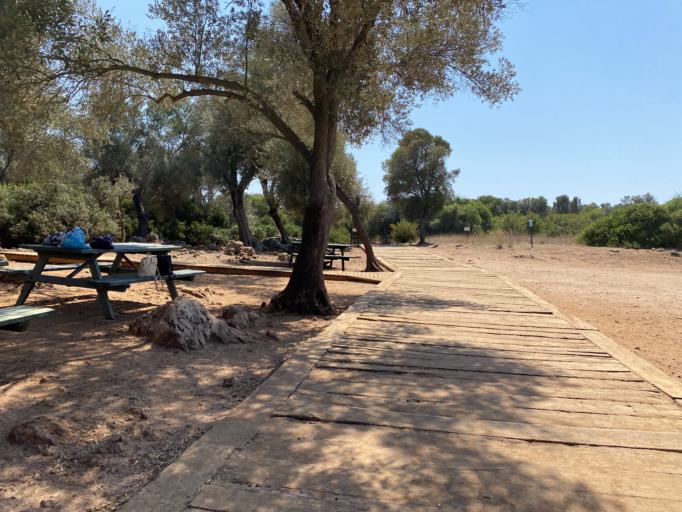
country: TR
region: Mugla
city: Yerkesik
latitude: 36.9926
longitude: 28.2036
